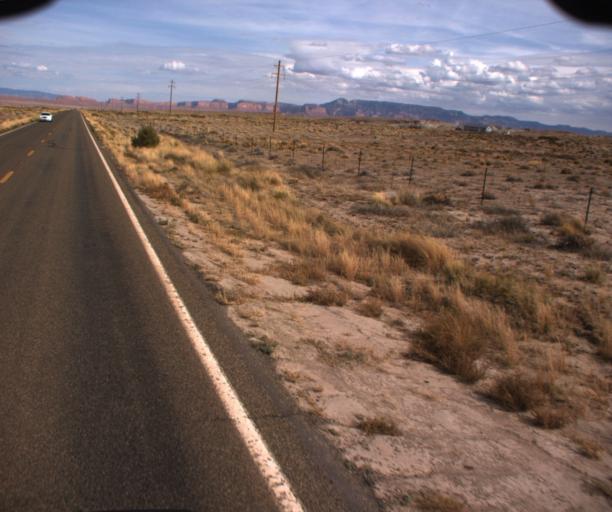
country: US
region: Arizona
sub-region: Apache County
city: Many Farms
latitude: 36.4778
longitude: -109.5132
